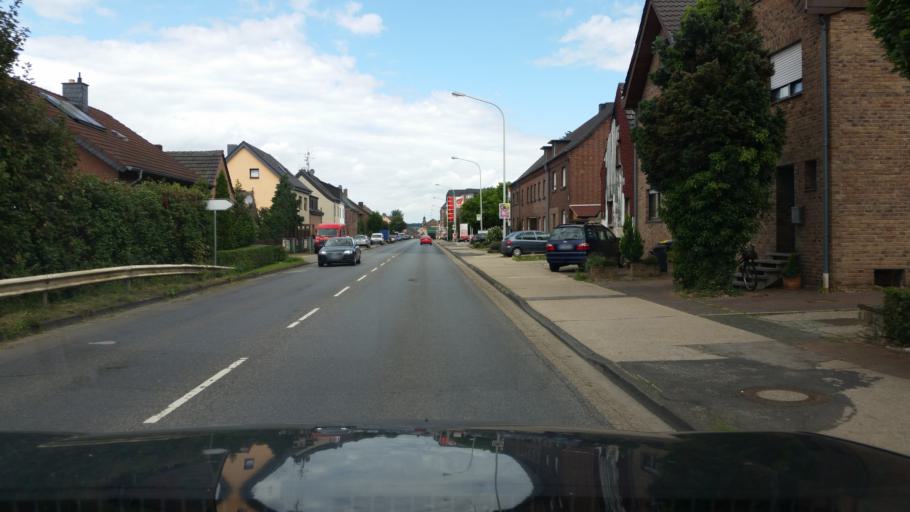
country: DE
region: North Rhine-Westphalia
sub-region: Regierungsbezirk Koln
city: Weilerswist
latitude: 50.7490
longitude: 6.8378
